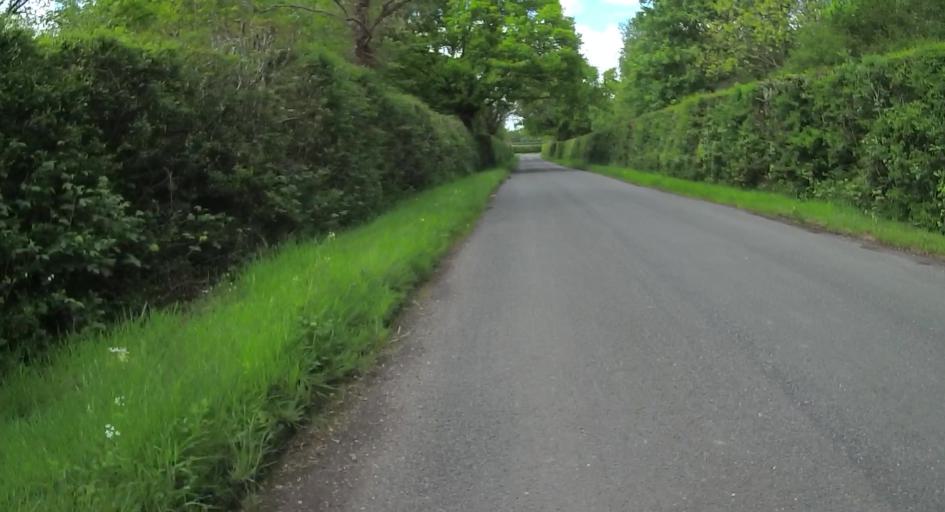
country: GB
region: England
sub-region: West Berkshire
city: Stratfield Mortimer
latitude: 51.3525
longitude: -1.0063
